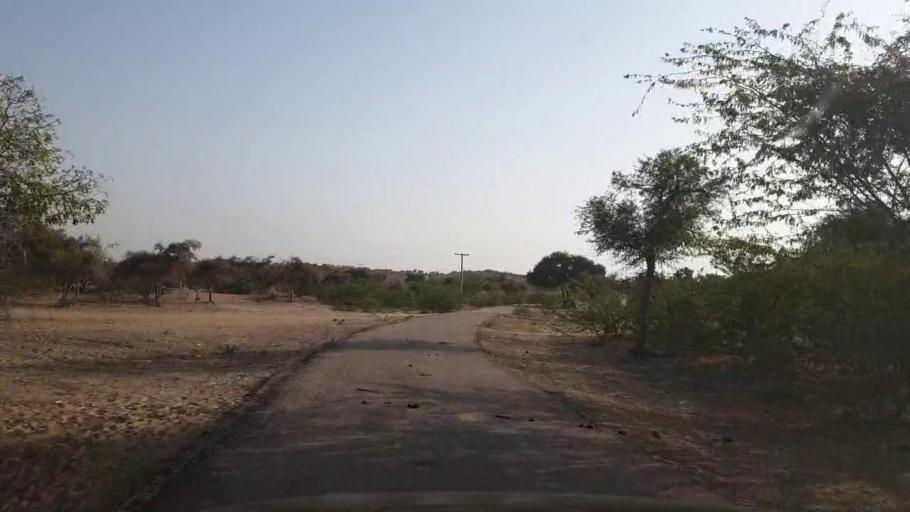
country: PK
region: Sindh
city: Islamkot
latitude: 25.1004
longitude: 70.3696
